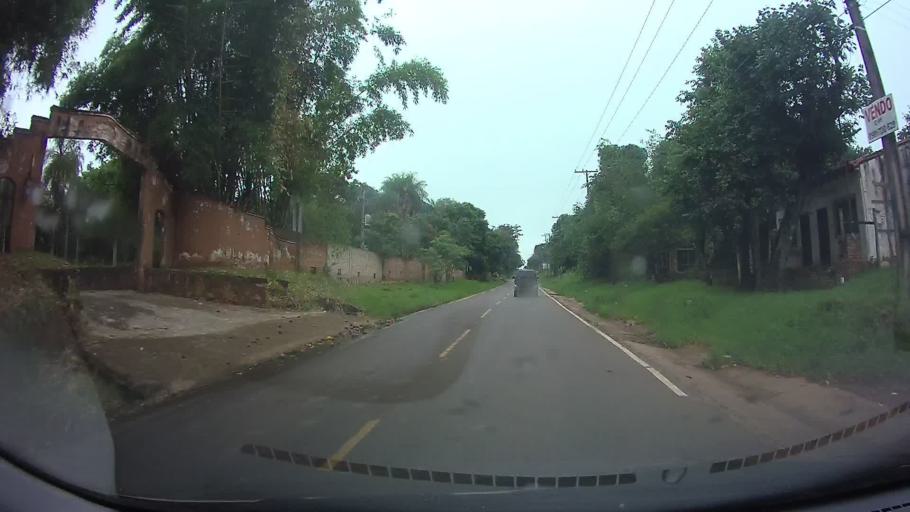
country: PY
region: Central
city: Itaugua
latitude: -25.3683
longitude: -57.3471
